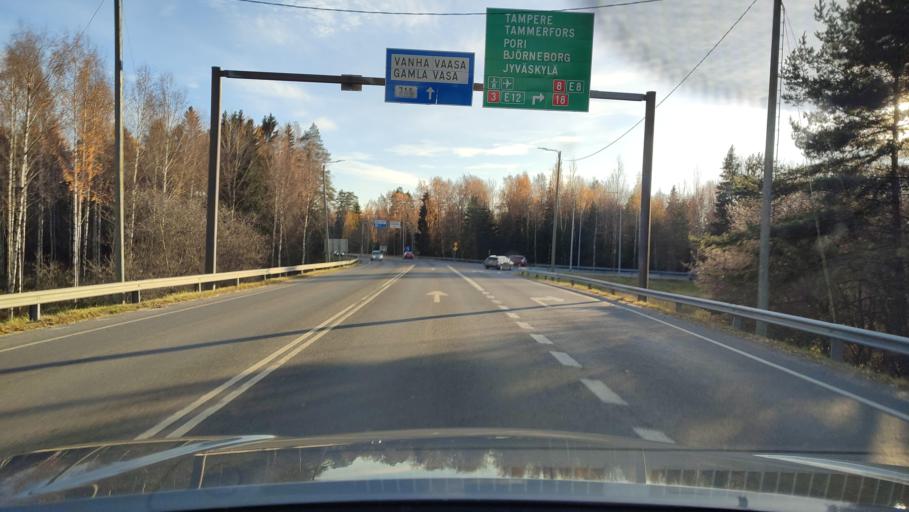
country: FI
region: Ostrobothnia
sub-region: Vaasa
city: Teeriniemi
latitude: 63.0728
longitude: 21.6841
